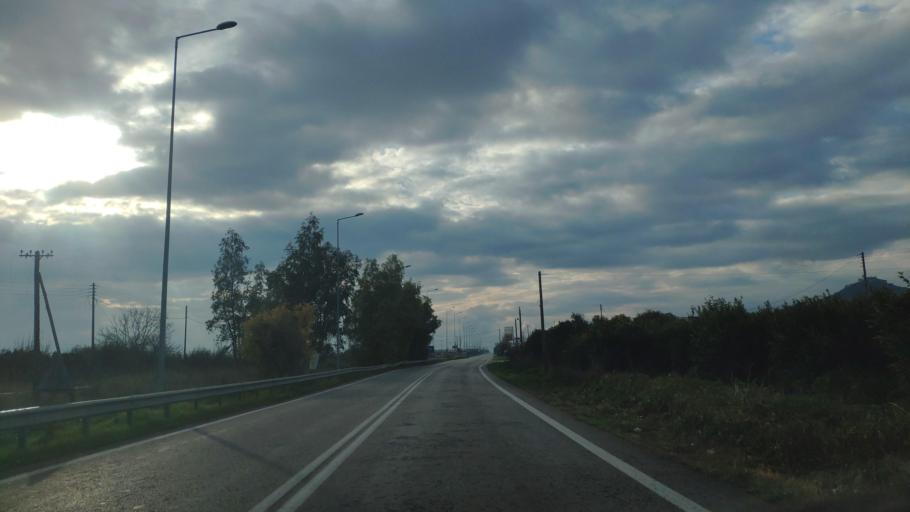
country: GR
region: Peloponnese
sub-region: Nomos Argolidos
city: Koutsopodi
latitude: 37.6660
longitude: 22.7237
